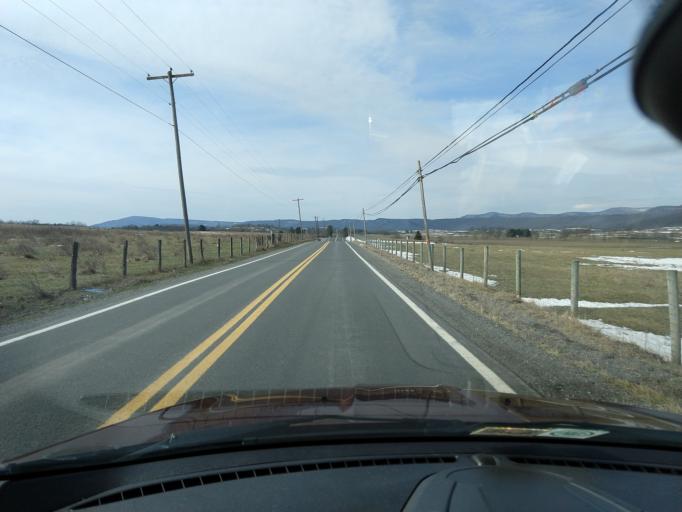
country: US
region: West Virginia
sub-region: Pocahontas County
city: Marlinton
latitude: 38.1517
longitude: -80.1863
